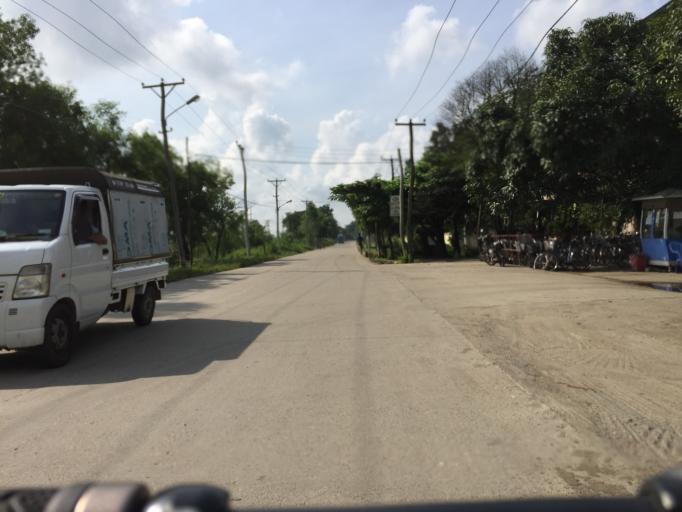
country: MM
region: Yangon
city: Syriam
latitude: 16.8312
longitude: 96.2222
